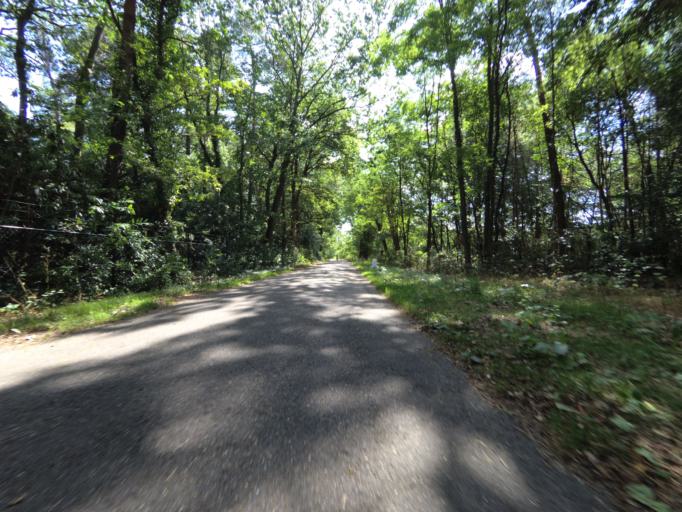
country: NL
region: Overijssel
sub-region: Gemeente Hengelo
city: Hengelo
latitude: 52.2465
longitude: 6.8398
